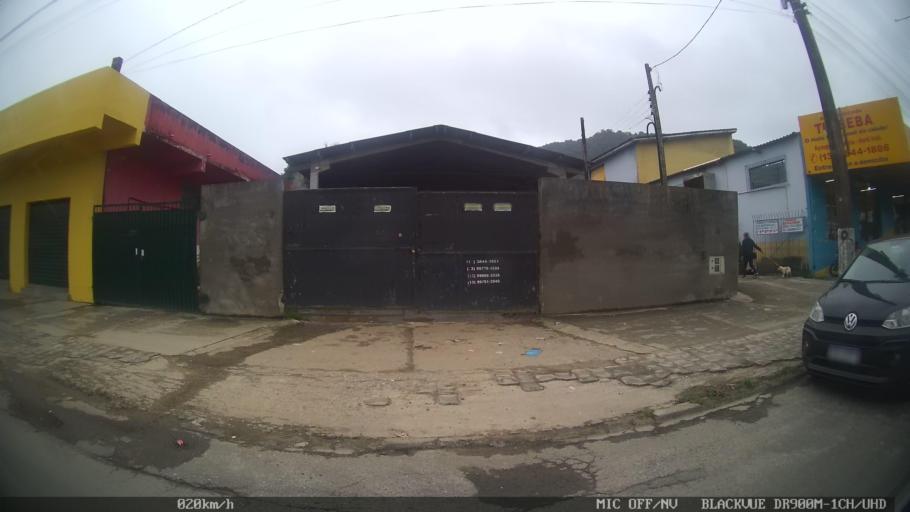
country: BR
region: Sao Paulo
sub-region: Juquia
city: Juquia
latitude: -24.3135
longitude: -47.6291
